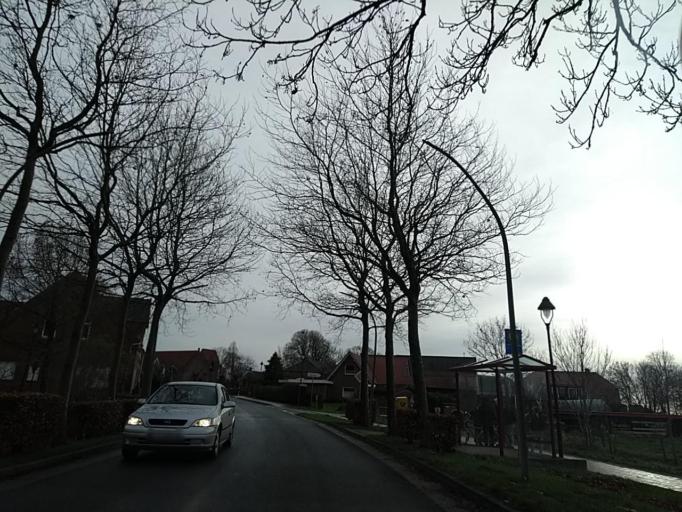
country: DE
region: Lower Saxony
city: Jemgum
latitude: 53.2907
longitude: 7.3563
